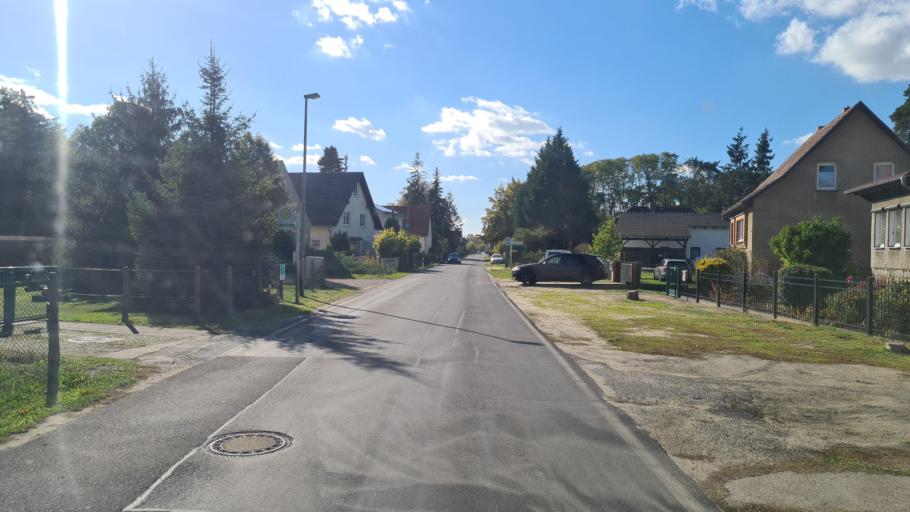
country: DE
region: Brandenburg
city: Kolkwitz
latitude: 51.7612
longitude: 14.2571
